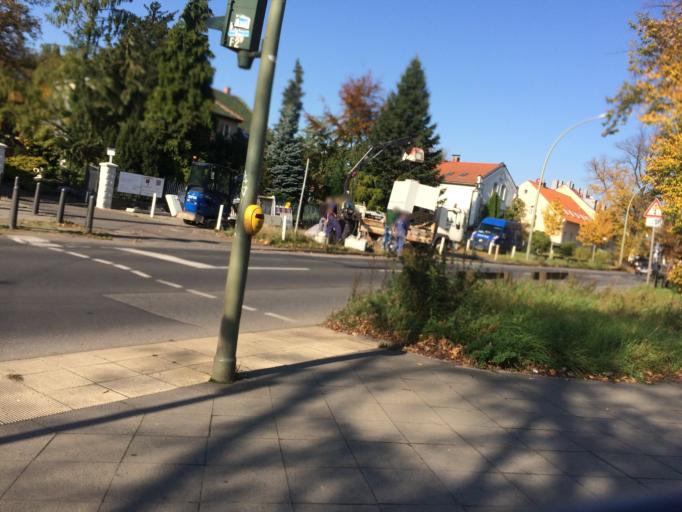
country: DE
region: Berlin
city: Buchholz
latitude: 52.6077
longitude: 13.4337
